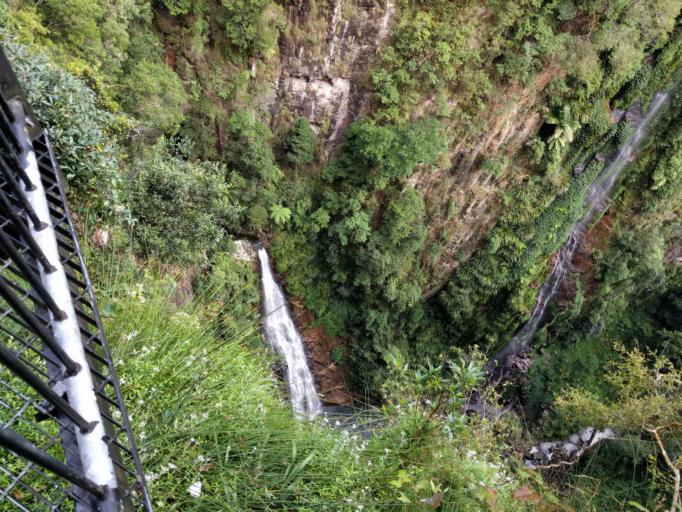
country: AU
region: Queensland
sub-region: Gold Coast
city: Tallebudgera Valley
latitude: -28.2336
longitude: 153.1910
